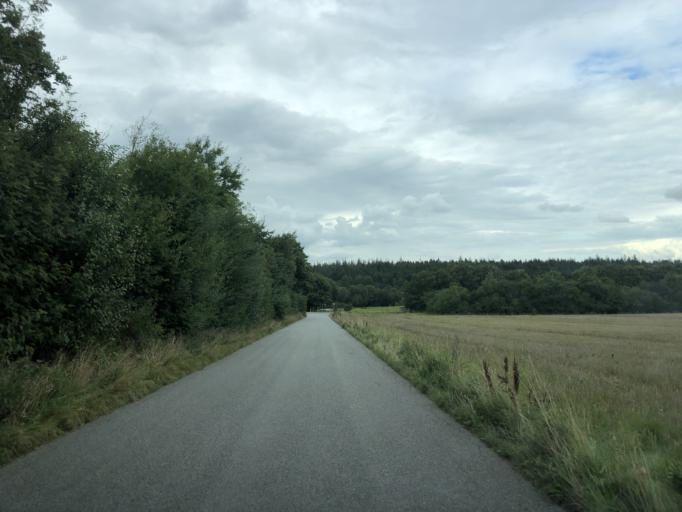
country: DK
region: Central Jutland
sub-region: Holstebro Kommune
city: Ulfborg
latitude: 56.1999
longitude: 8.4238
